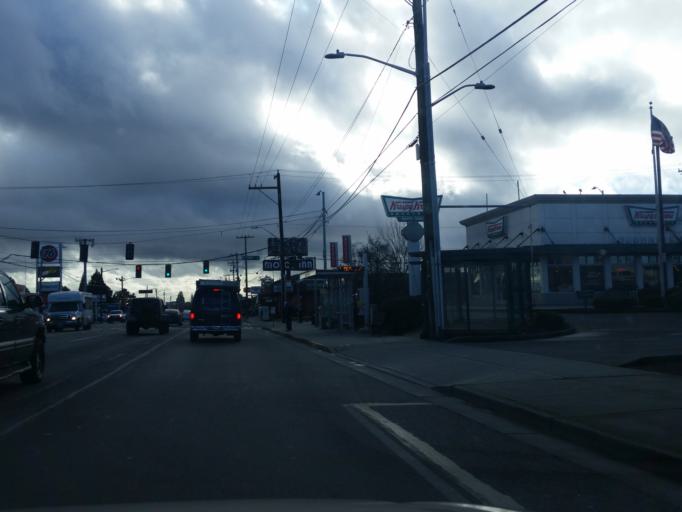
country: US
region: Washington
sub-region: King County
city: Shoreline
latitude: 47.7202
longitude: -122.3451
